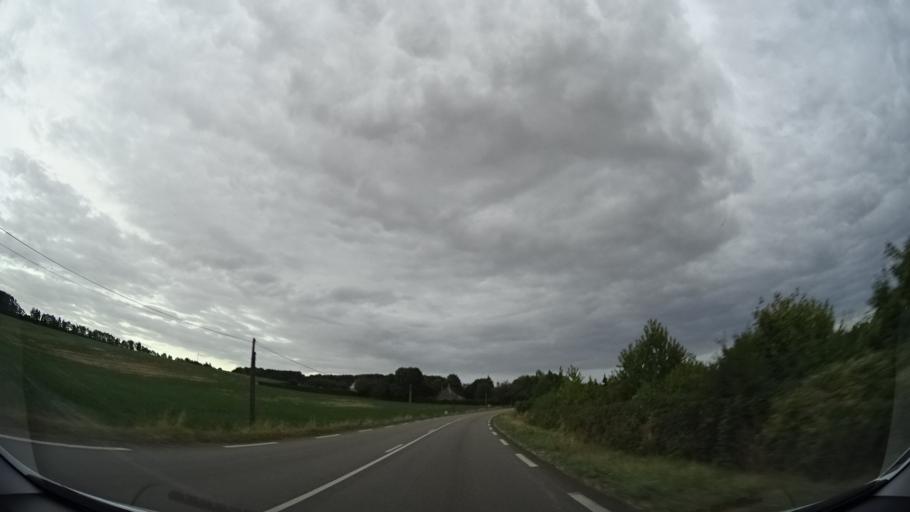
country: FR
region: Centre
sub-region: Departement du Loiret
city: Douchy
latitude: 47.9351
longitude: 3.0913
